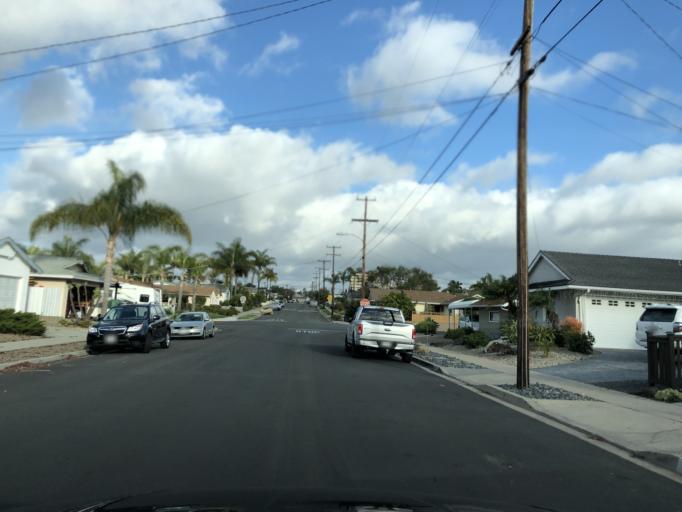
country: US
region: California
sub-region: San Diego County
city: La Jolla
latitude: 32.8178
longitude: -117.1895
